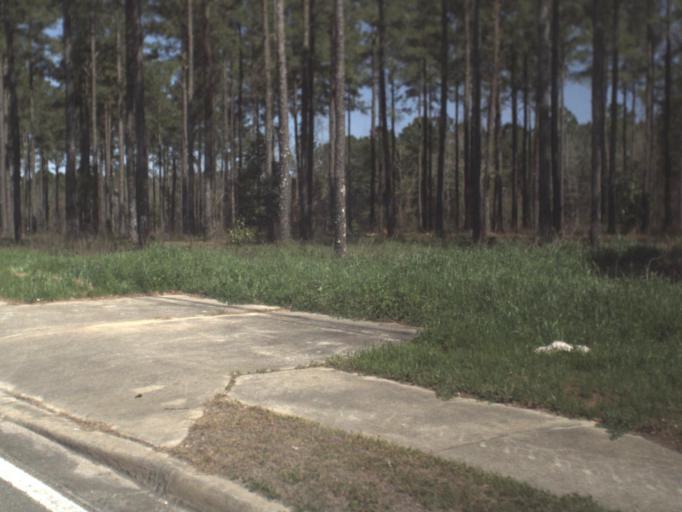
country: US
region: Florida
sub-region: Gadsden County
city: Quincy
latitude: 30.5649
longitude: -84.5927
